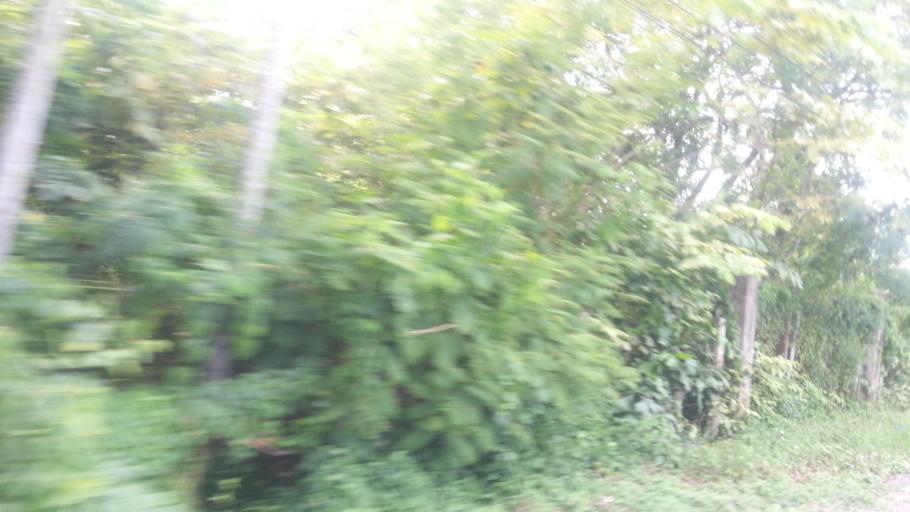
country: TH
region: Pathum Thani
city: Nong Suea
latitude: 14.1468
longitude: 100.8233
